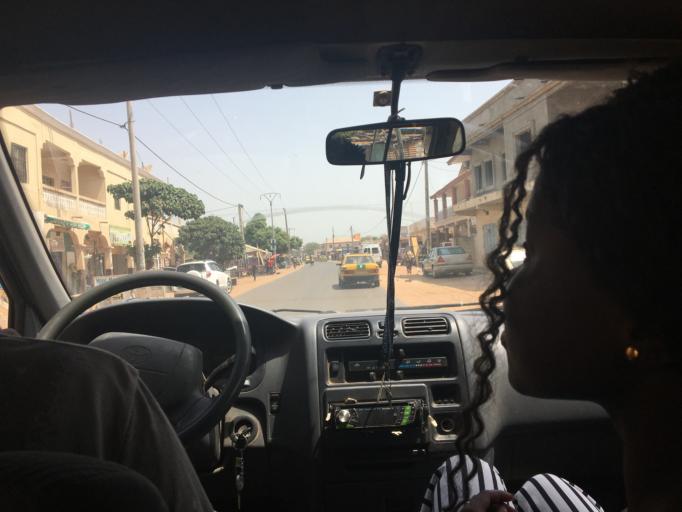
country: GM
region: Western
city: Abuko
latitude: 13.3895
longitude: -16.6757
